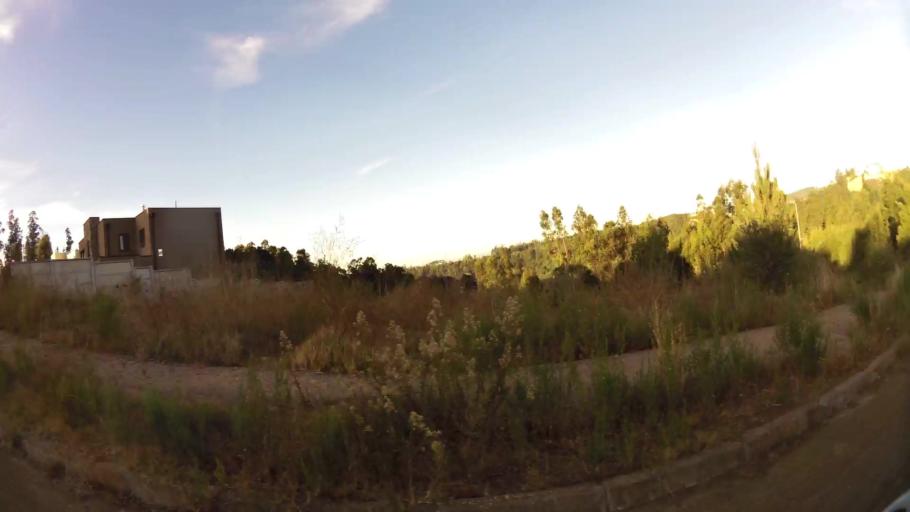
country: CL
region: Biobio
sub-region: Provincia de Concepcion
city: Concepcion
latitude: -36.8524
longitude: -73.0899
